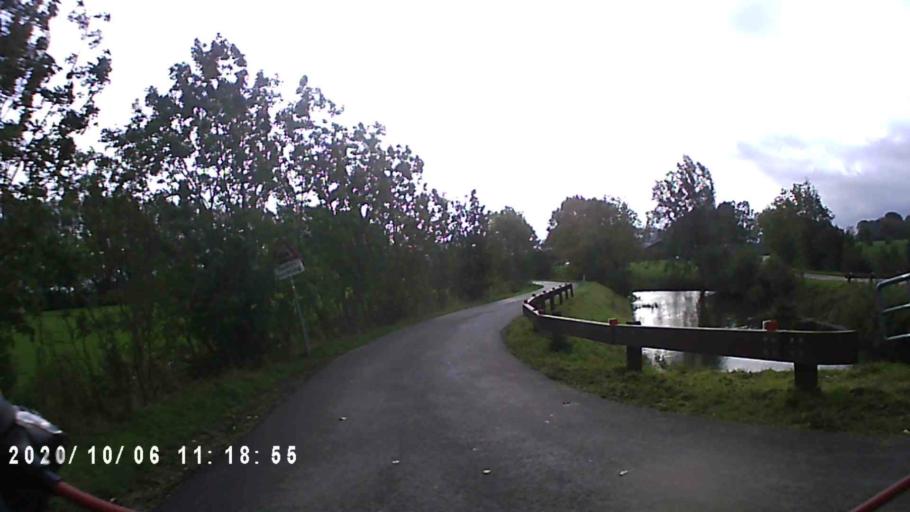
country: NL
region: Groningen
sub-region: Gemeente Zuidhorn
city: Oldehove
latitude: 53.3506
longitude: 6.3923
